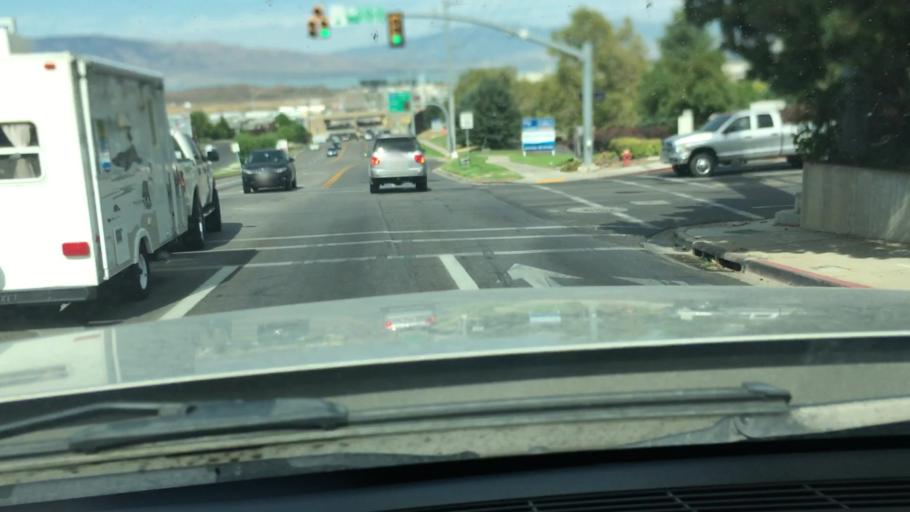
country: US
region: Utah
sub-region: Utah County
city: Lindon
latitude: 40.3264
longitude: -111.7247
